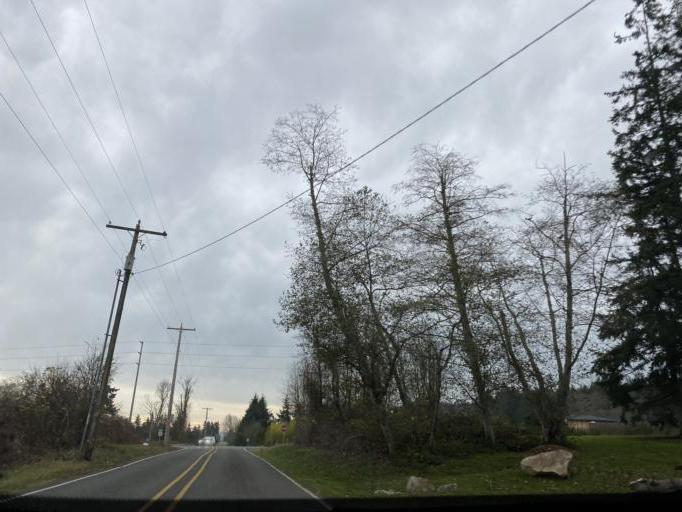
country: US
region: Washington
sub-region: Island County
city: Freeland
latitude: 48.0099
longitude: -122.5069
